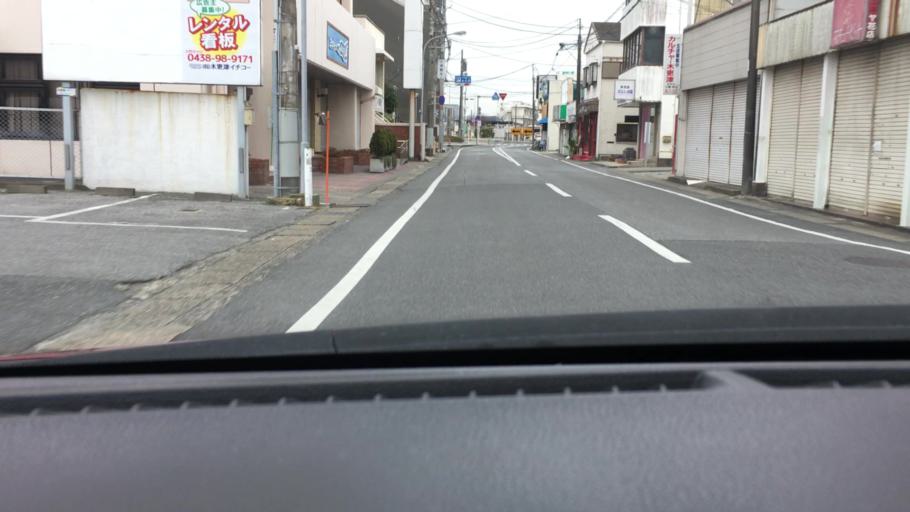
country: JP
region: Chiba
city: Kisarazu
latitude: 35.3830
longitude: 139.9255
